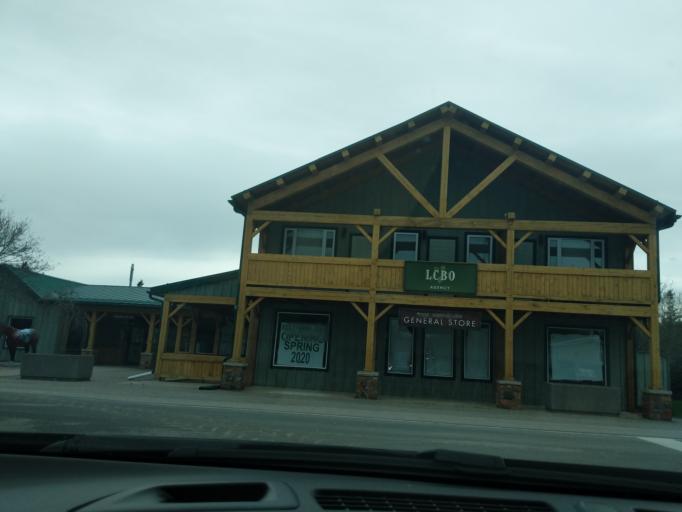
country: CA
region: Ontario
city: Orangeville
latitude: 44.0216
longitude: -79.9691
